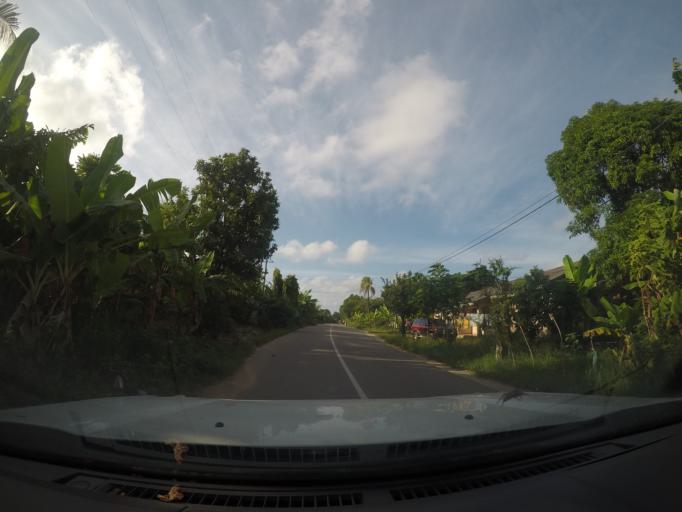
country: TZ
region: Pemba South
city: Chake Chake
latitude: -5.2460
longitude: 39.7826
